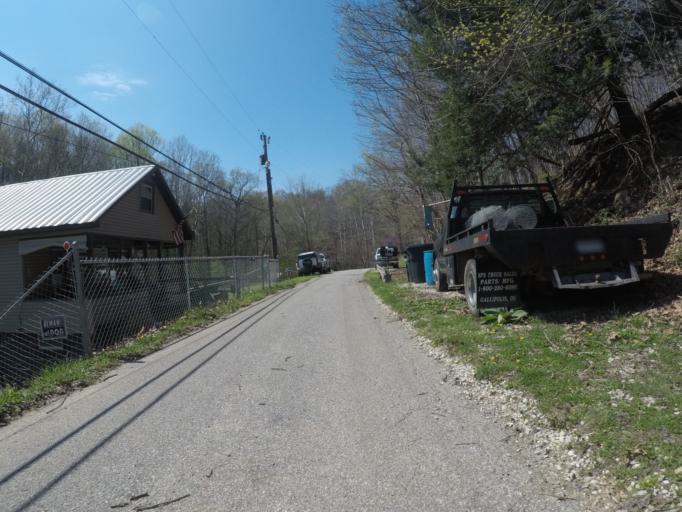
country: US
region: Ohio
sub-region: Lawrence County
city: Burlington
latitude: 38.3929
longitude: -82.5271
